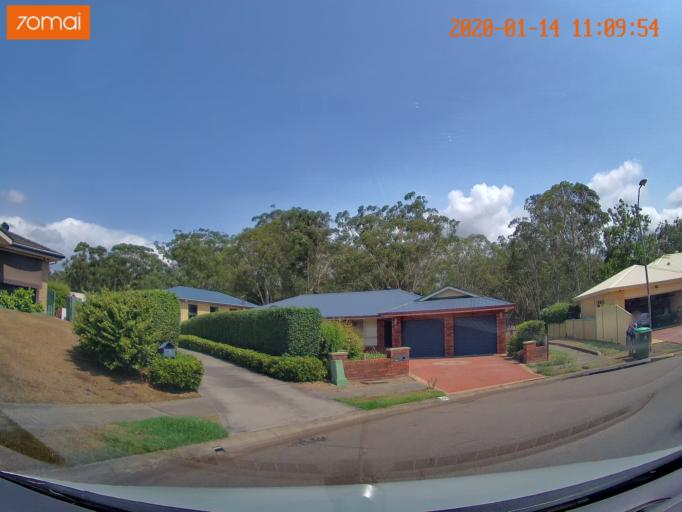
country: AU
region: New South Wales
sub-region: Lake Macquarie Shire
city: Dora Creek
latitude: -33.0952
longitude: 151.4770
